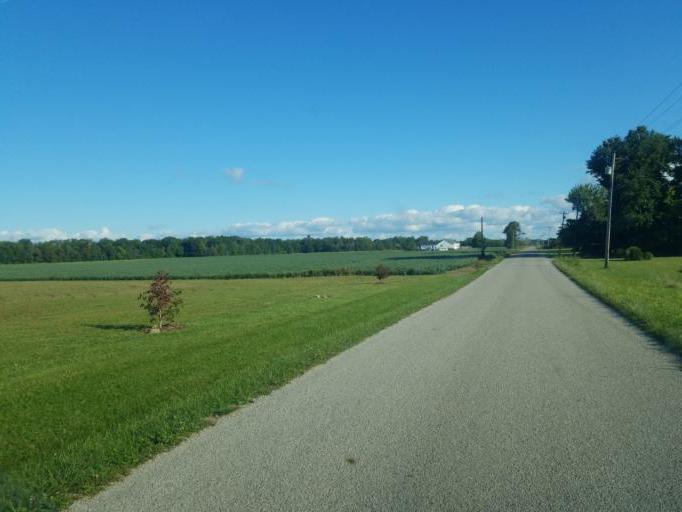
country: US
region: Ohio
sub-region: Lorain County
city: Camden
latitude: 41.2253
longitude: -82.3210
